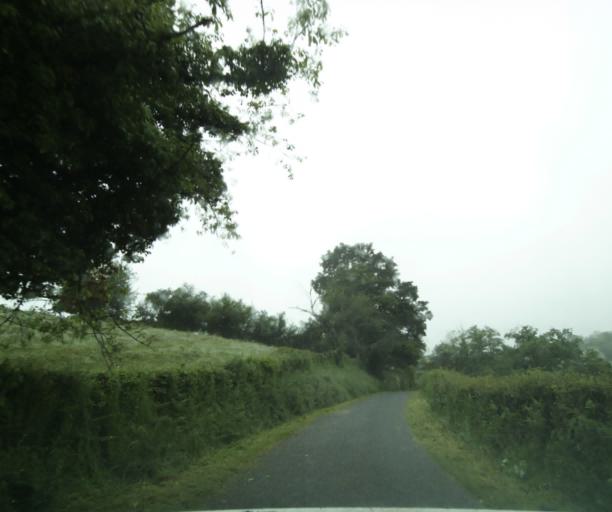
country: FR
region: Bourgogne
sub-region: Departement de Saone-et-Loire
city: Charolles
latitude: 46.4072
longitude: 4.3902
